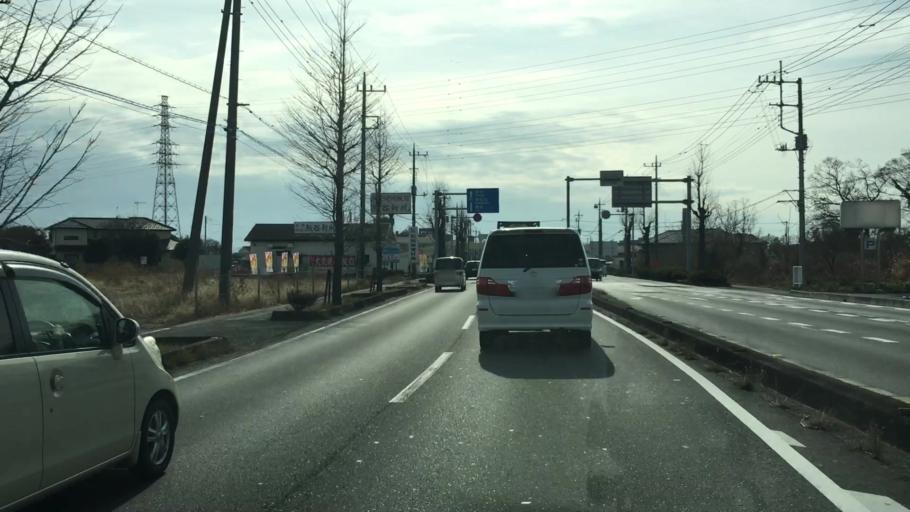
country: JP
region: Saitama
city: Kumagaya
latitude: 36.1716
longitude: 139.3704
